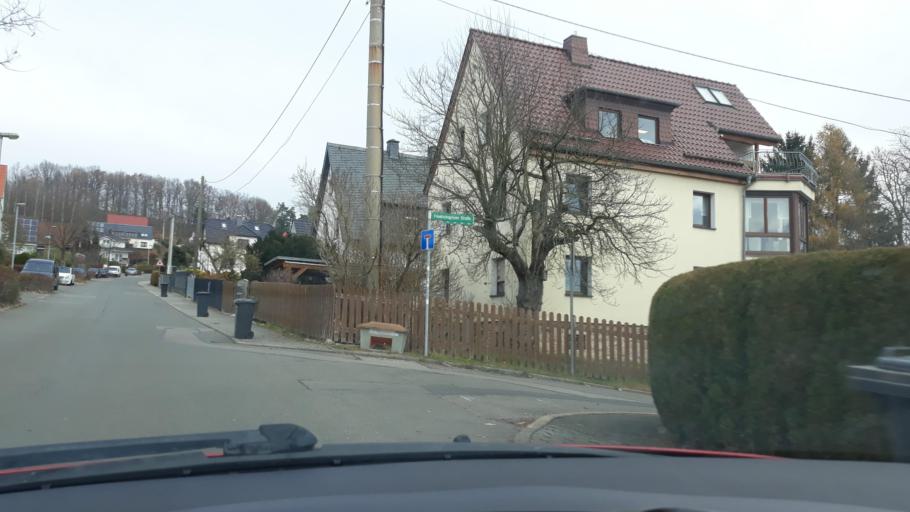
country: DE
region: Saxony
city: Wilkau-Hasslau
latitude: 50.6674
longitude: 12.5481
